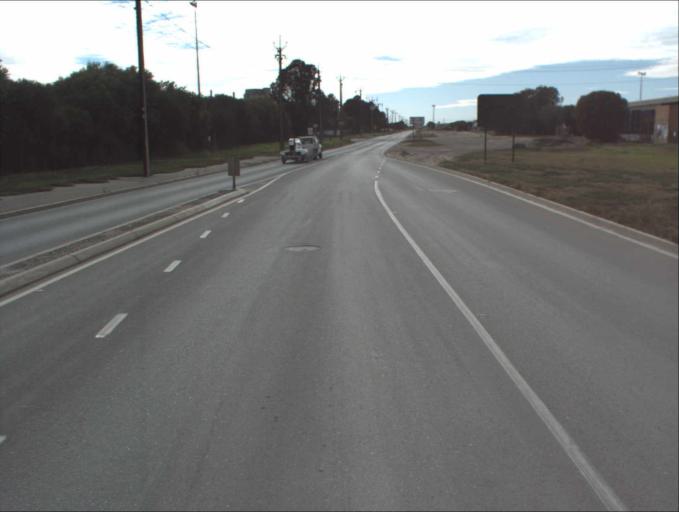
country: AU
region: South Australia
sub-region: Port Adelaide Enfield
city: Birkenhead
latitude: -34.8355
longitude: 138.5151
